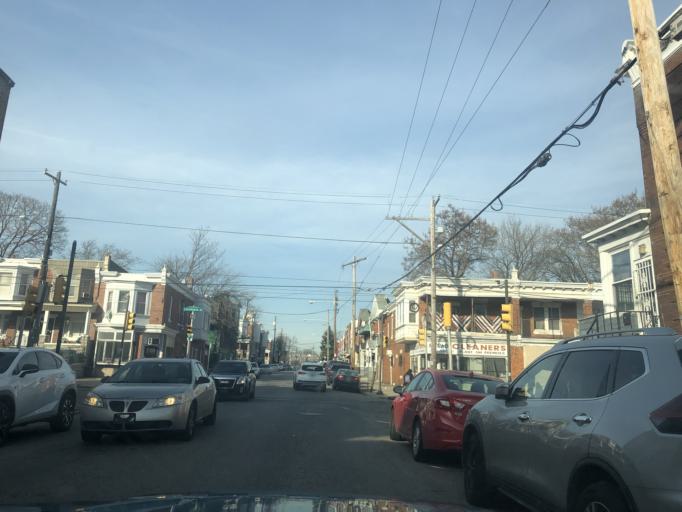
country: US
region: Pennsylvania
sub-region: Delaware County
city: Millbourne
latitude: 39.9764
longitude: -75.2336
